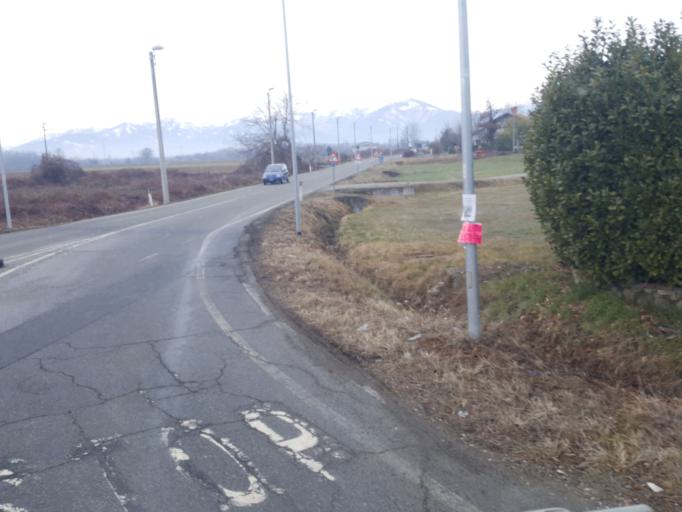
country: IT
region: Piedmont
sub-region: Provincia di Torino
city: Aglie
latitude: 45.3594
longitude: 7.7652
